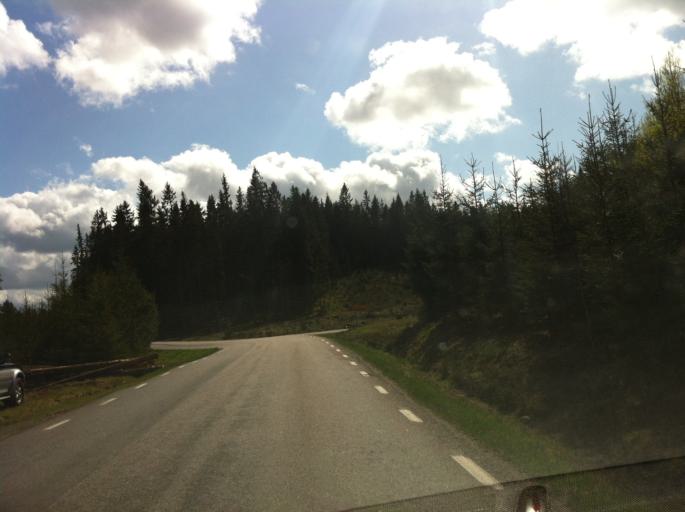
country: SE
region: Vaestra Goetaland
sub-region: Bollebygds Kommun
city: Bollebygd
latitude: 57.8098
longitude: 12.6389
